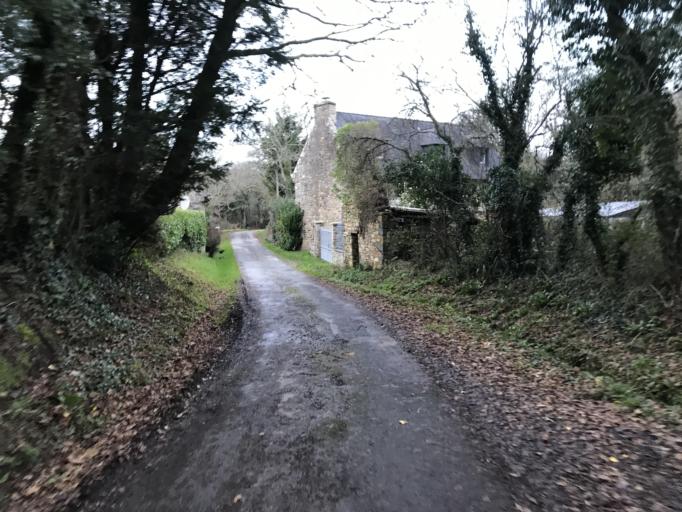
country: FR
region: Brittany
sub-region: Departement du Finistere
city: Loperhet
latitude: 48.3616
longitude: -4.3167
